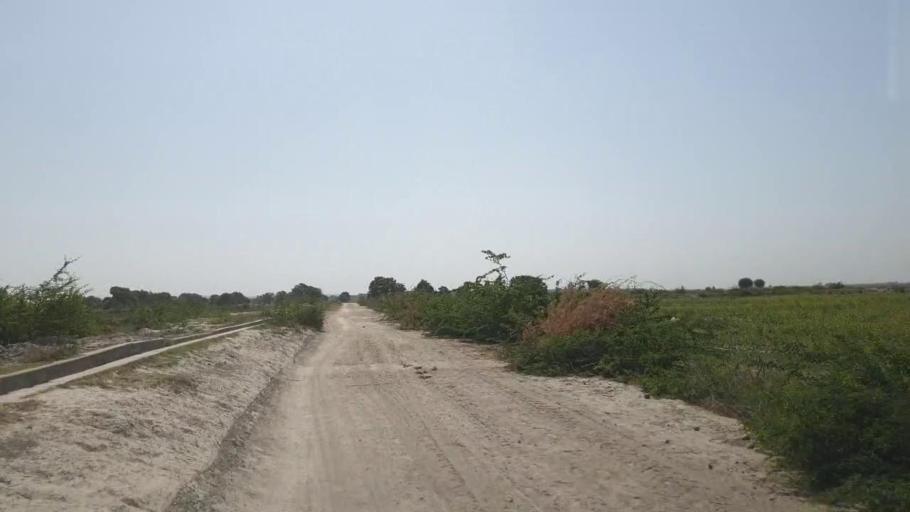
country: PK
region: Sindh
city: Naukot
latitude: 24.9007
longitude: 69.4875
